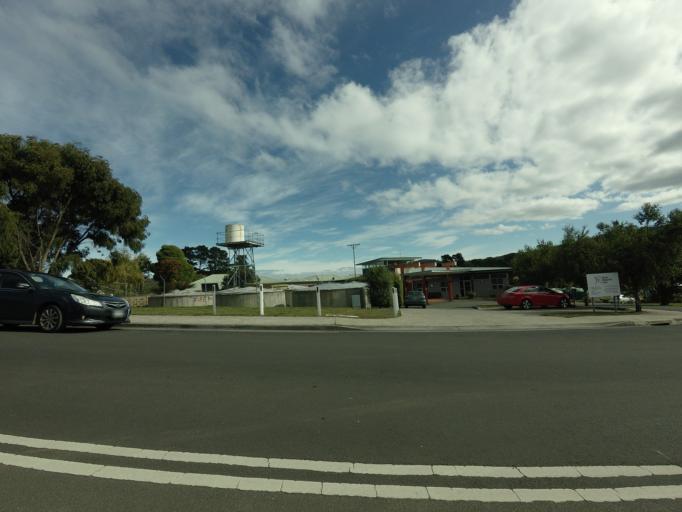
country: AU
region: Tasmania
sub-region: Clarence
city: Sandford
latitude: -43.0966
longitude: 147.7435
